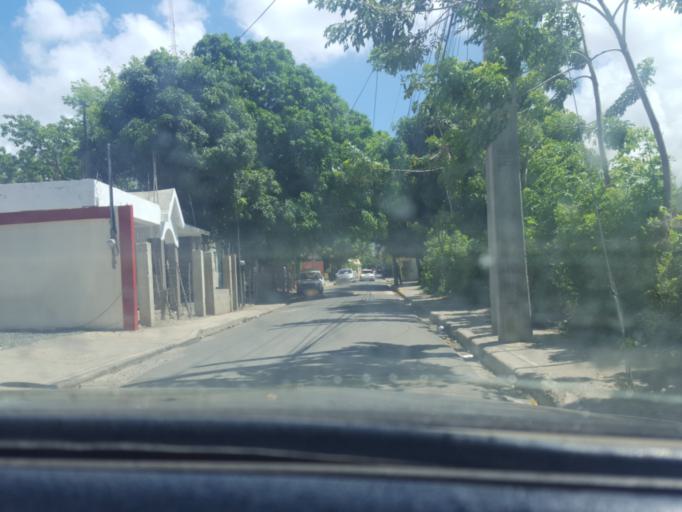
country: DO
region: Santiago
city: Santiago de los Caballeros
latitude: 19.4882
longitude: -70.6961
